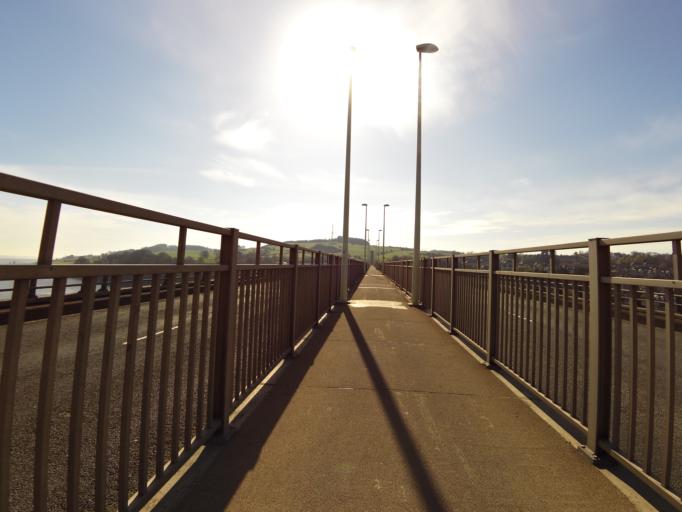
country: GB
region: Scotland
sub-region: Fife
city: Newport-On-Tay
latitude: 56.4489
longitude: -2.9378
